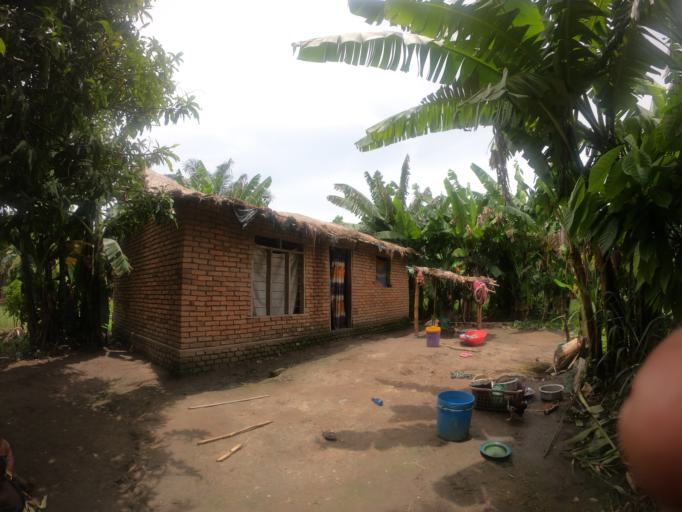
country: TZ
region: Mbeya
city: Kyela
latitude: -9.6441
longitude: 33.8179
